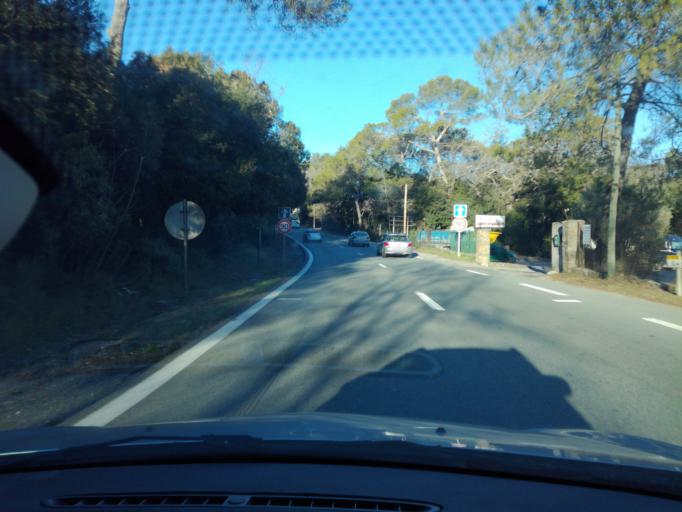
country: FR
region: Provence-Alpes-Cote d'Azur
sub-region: Departement des Alpes-Maritimes
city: Vallauris
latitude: 43.6088
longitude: 7.0543
